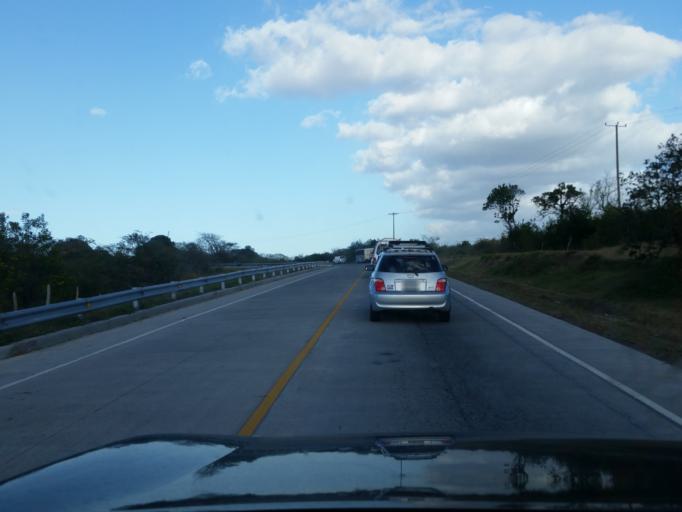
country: NI
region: Managua
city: Ciudad Sandino
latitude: 12.0754
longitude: -86.4285
